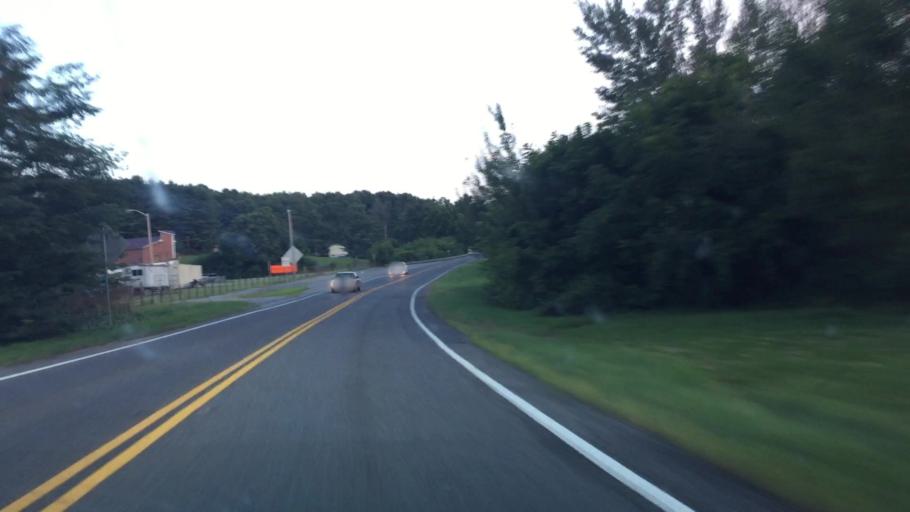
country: US
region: Virginia
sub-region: Wythe County
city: Wytheville
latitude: 36.9396
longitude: -80.9440
